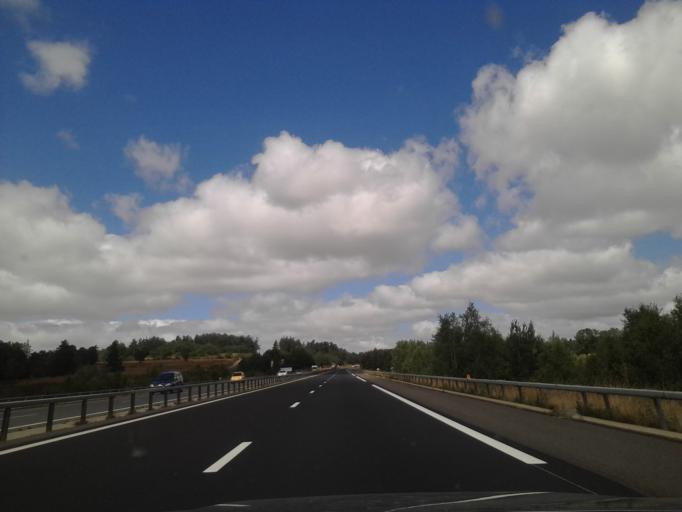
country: FR
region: Languedoc-Roussillon
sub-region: Departement de la Lozere
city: Le Malzieu-Ville
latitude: 44.8166
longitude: 3.2800
